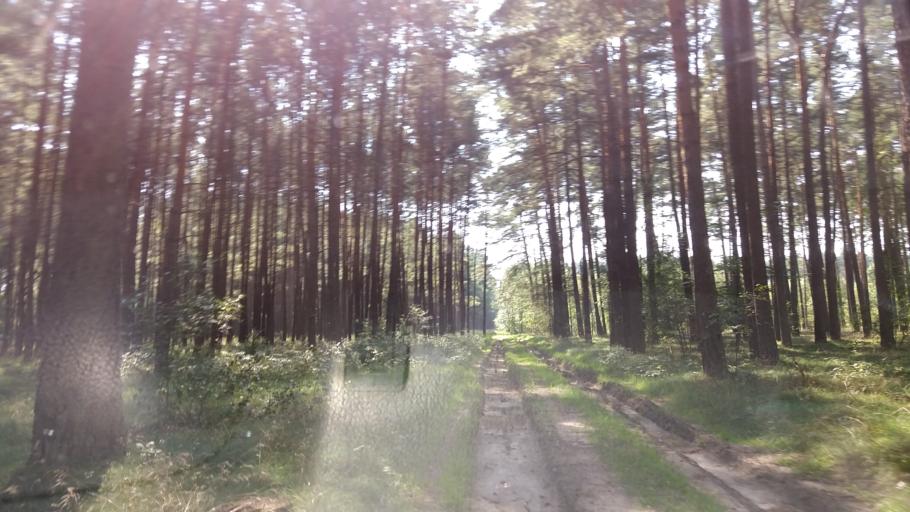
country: PL
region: West Pomeranian Voivodeship
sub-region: Powiat walecki
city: Tuczno
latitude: 53.2180
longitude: 16.0194
